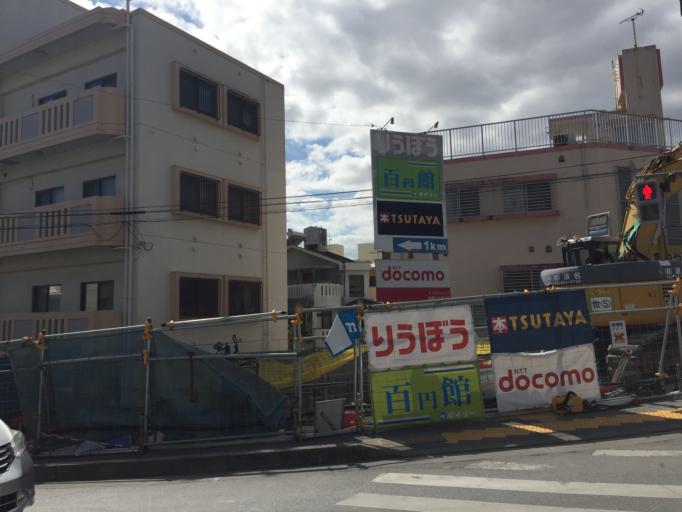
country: JP
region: Okinawa
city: Ginowan
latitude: 26.2341
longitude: 127.7286
